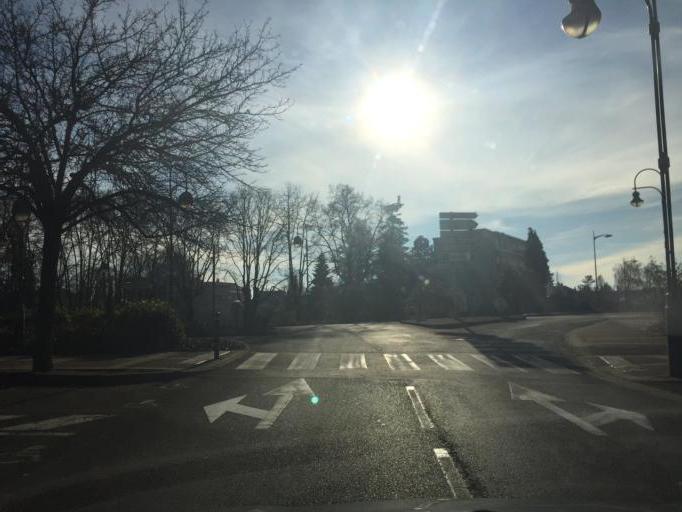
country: FR
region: Bourgogne
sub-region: Departement de Saone-et-Loire
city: Paray-le-Monial
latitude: 46.4517
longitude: 4.1171
